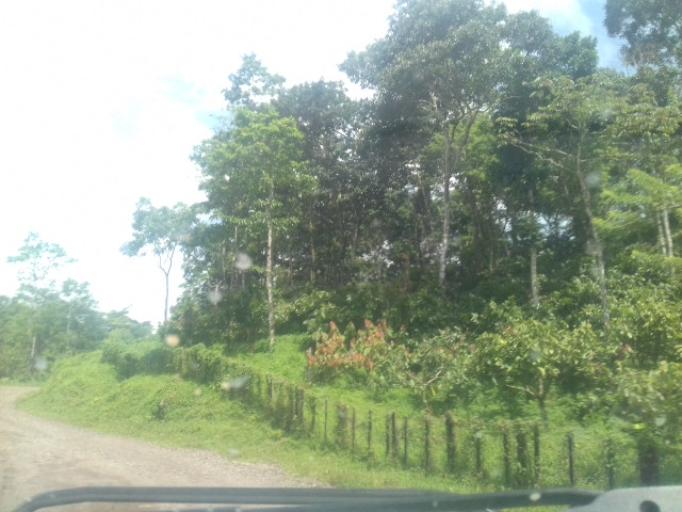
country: NI
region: Matagalpa
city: Matiguas
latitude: 12.9328
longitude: -85.3667
